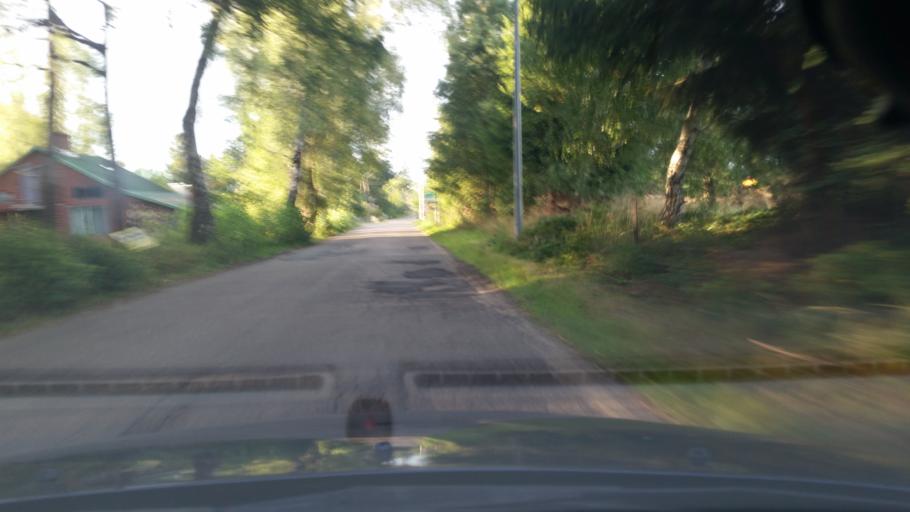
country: PL
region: Pomeranian Voivodeship
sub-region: Powiat wejherowski
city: Choczewo
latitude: 54.7667
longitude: 17.7934
